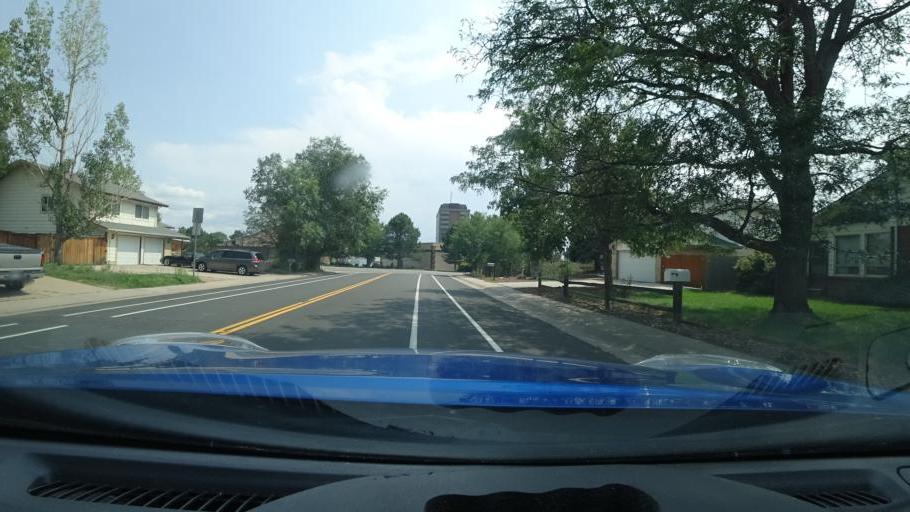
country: US
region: Colorado
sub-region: Adams County
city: Aurora
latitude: 39.6682
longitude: -104.8608
